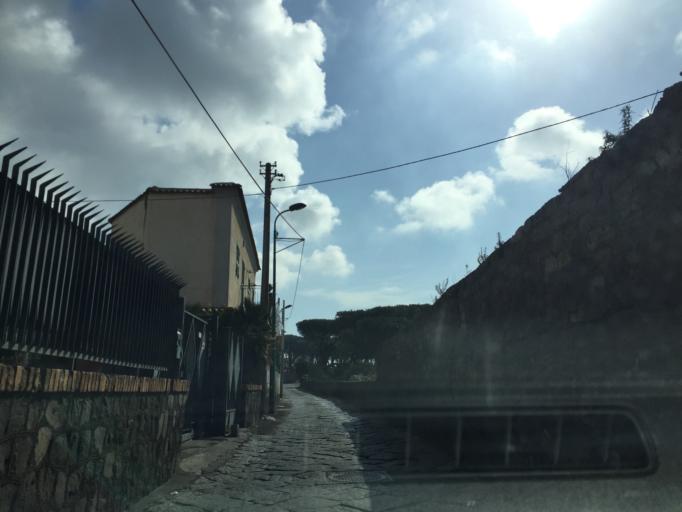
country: IT
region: Campania
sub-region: Provincia di Napoli
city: Torre del Greco
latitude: 40.7801
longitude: 14.4087
